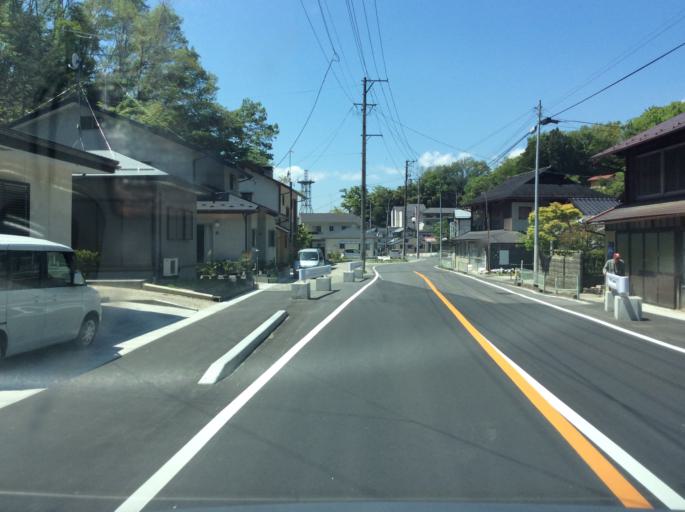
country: JP
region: Fukushima
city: Miharu
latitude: 37.4392
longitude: 140.4961
